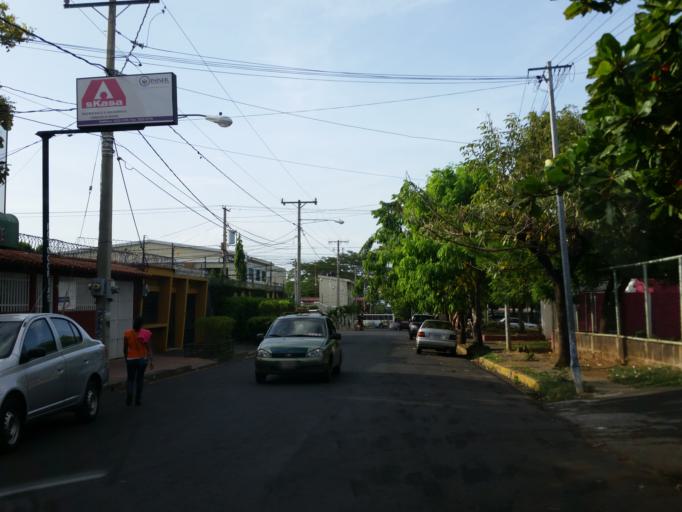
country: NI
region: Managua
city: Managua
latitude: 12.1447
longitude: -86.2781
